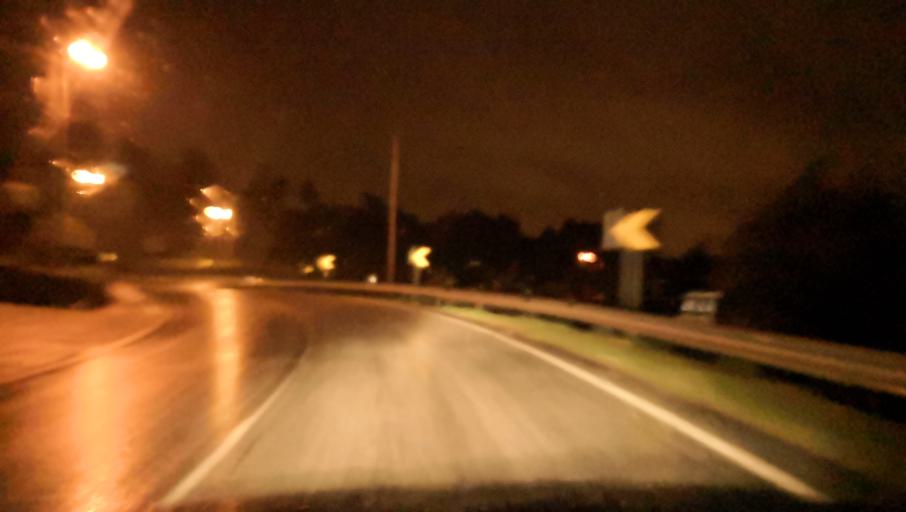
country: PT
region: Vila Real
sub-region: Vila Real
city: Vila Real
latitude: 41.3376
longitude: -7.7275
